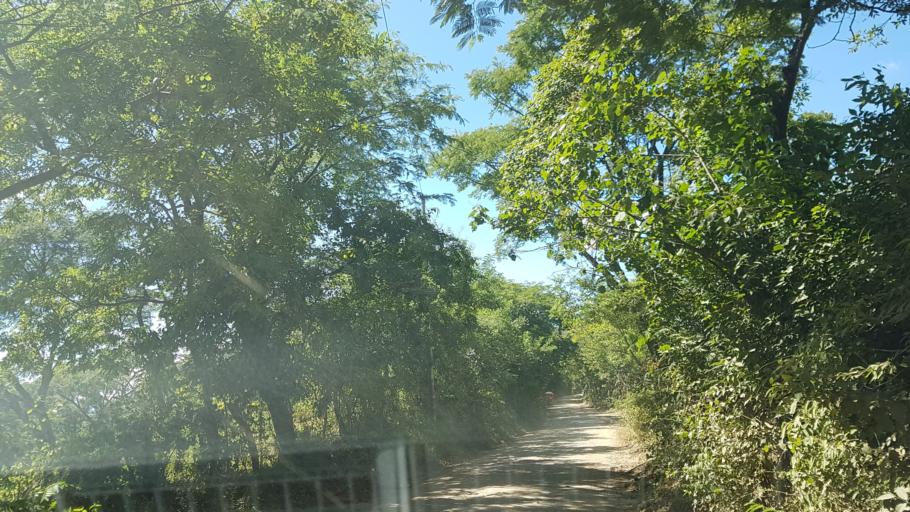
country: HN
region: El Paraiso
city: Santa Cruz
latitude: 13.7346
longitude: -86.6757
